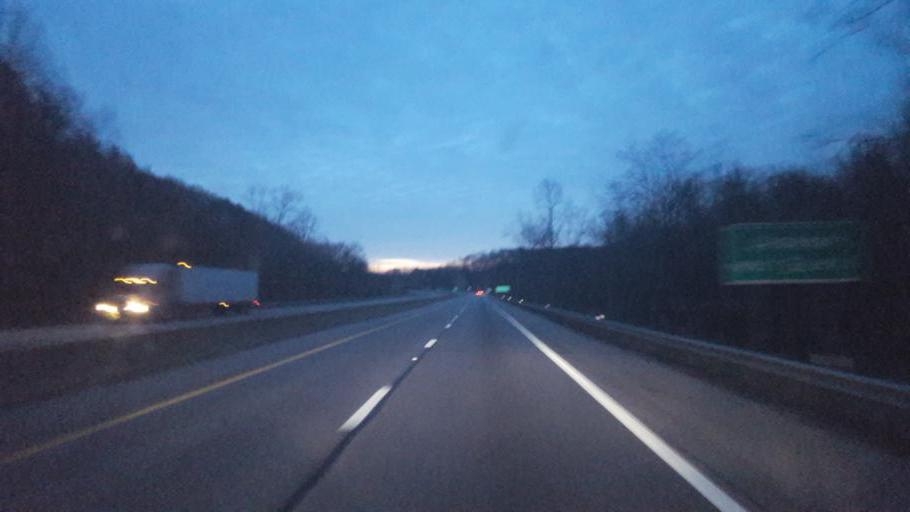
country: US
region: Ohio
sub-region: Jackson County
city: Jackson
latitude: 39.1026
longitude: -82.6711
